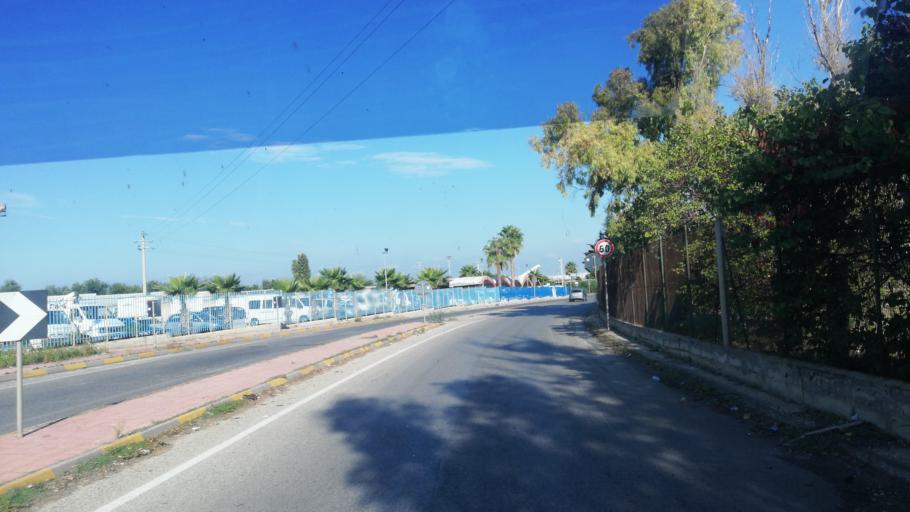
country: IT
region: Apulia
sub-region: Provincia di Bari
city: Palo del Colle
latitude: 41.0686
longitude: 16.7035
